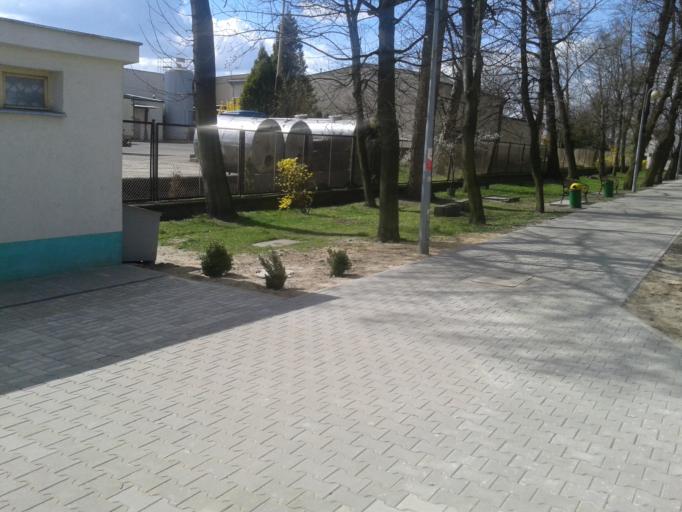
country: PL
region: Lower Silesian Voivodeship
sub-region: Powiat olesnicki
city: Miedzyborz
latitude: 51.3963
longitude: 17.6655
